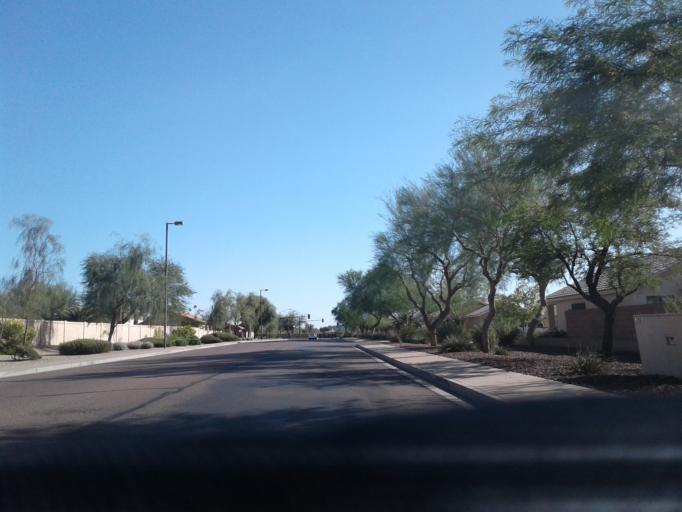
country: US
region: Arizona
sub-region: Maricopa County
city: Cave Creek
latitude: 33.6895
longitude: -112.0356
